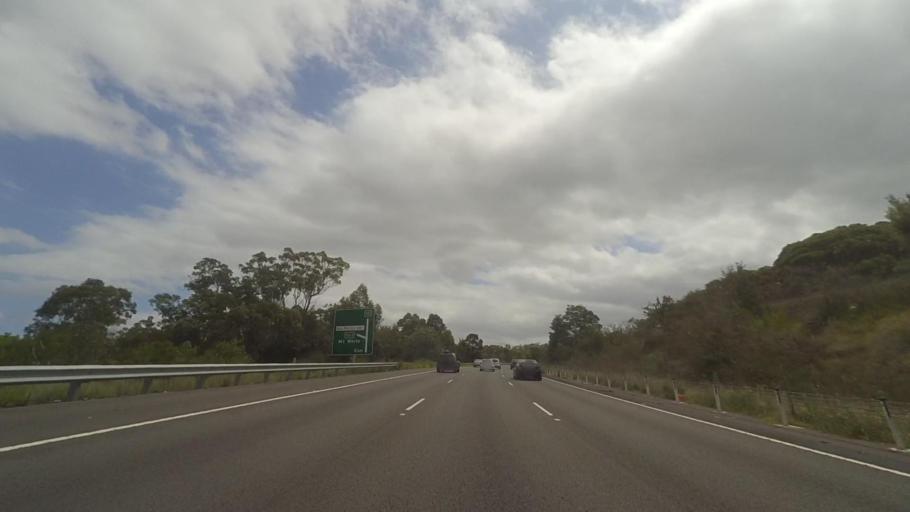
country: AU
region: New South Wales
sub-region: Gosford Shire
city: Point Clare
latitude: -33.4499
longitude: 151.2172
